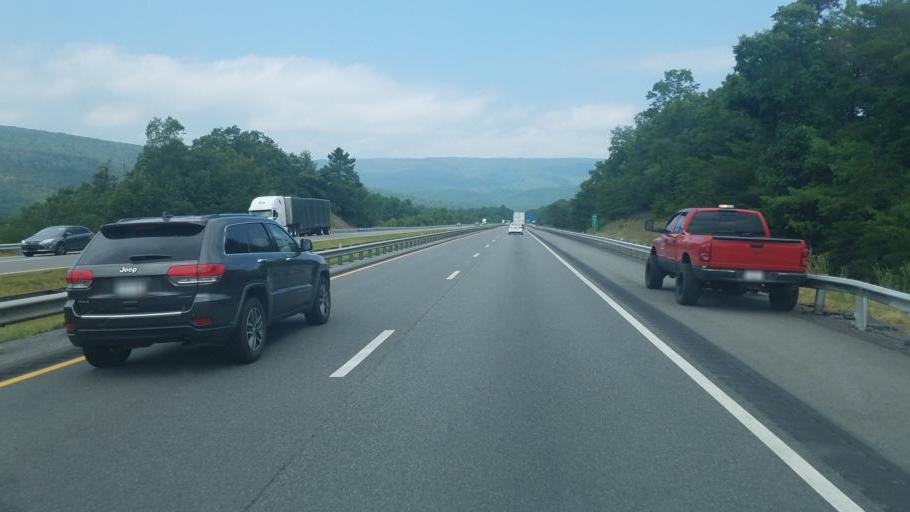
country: US
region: Virginia
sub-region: Bland County
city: Bland
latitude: 37.1493
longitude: -81.1400
